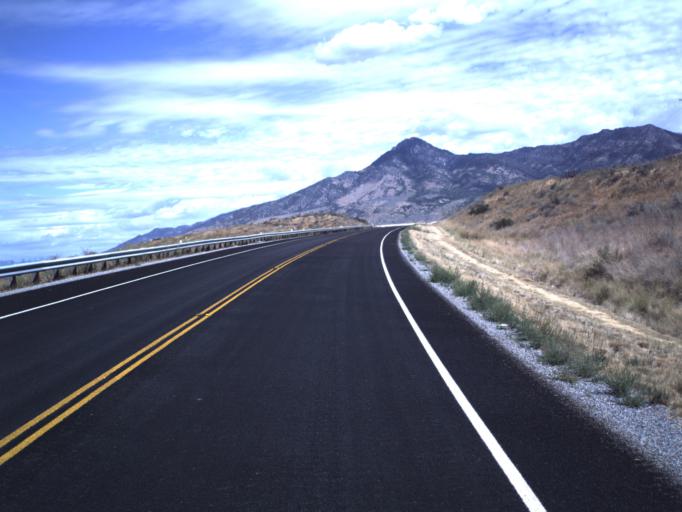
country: US
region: Utah
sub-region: Box Elder County
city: Garland
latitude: 41.8409
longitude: -112.1473
